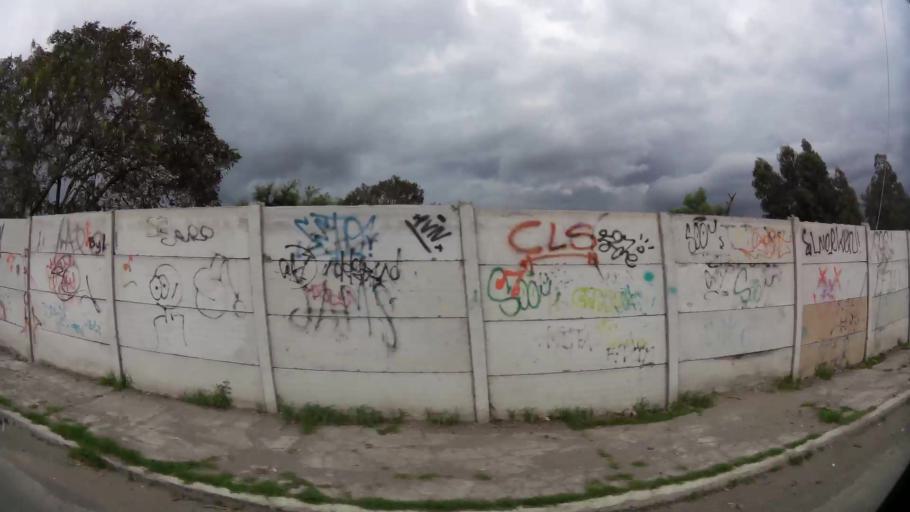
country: EC
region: Pichincha
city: Quito
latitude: -0.0172
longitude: -78.4517
